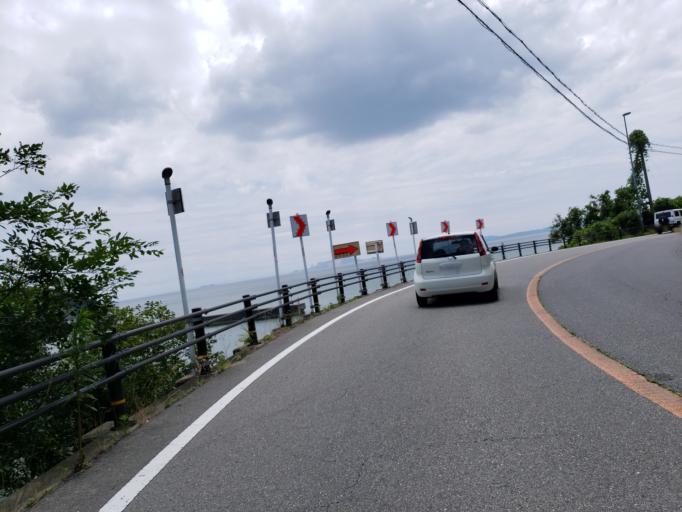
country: JP
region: Hyogo
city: Aioi
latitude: 34.7816
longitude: 134.5259
